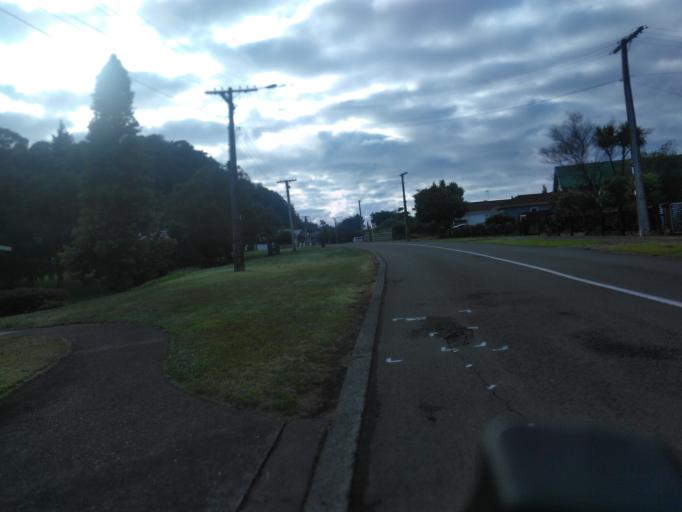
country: NZ
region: Gisborne
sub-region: Gisborne District
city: Gisborne
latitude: -38.6499
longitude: 178.0216
